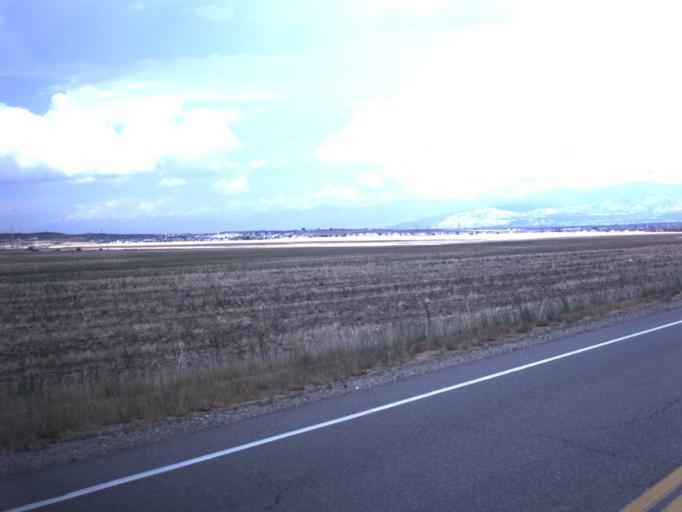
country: US
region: Utah
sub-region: Salt Lake County
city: Oquirrh
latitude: 40.5769
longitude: -112.0596
